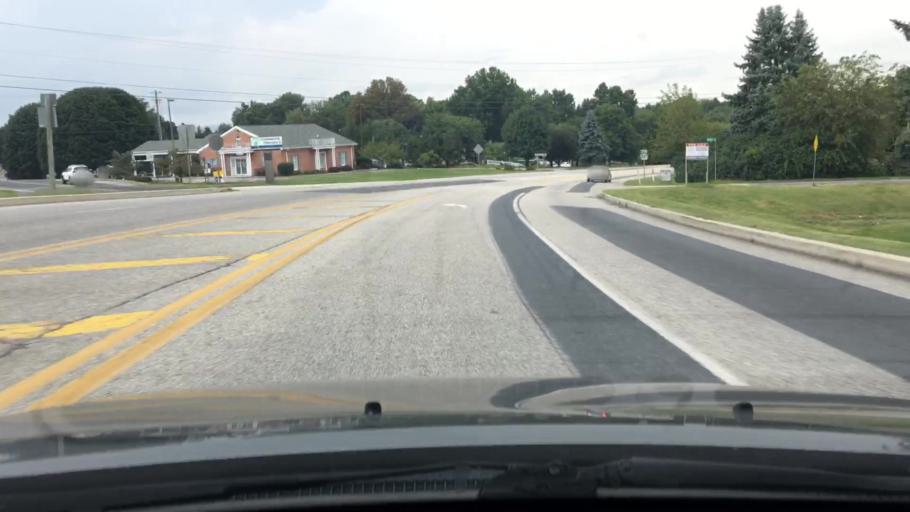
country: US
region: Pennsylvania
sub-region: Franklin County
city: Scotland
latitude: 39.9650
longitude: -77.5794
